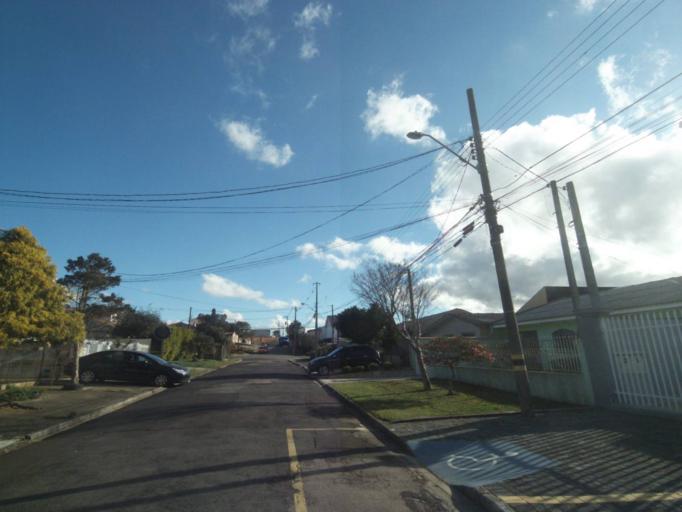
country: BR
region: Parana
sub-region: Sao Jose Dos Pinhais
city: Sao Jose dos Pinhais
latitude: -25.5261
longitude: -49.2846
